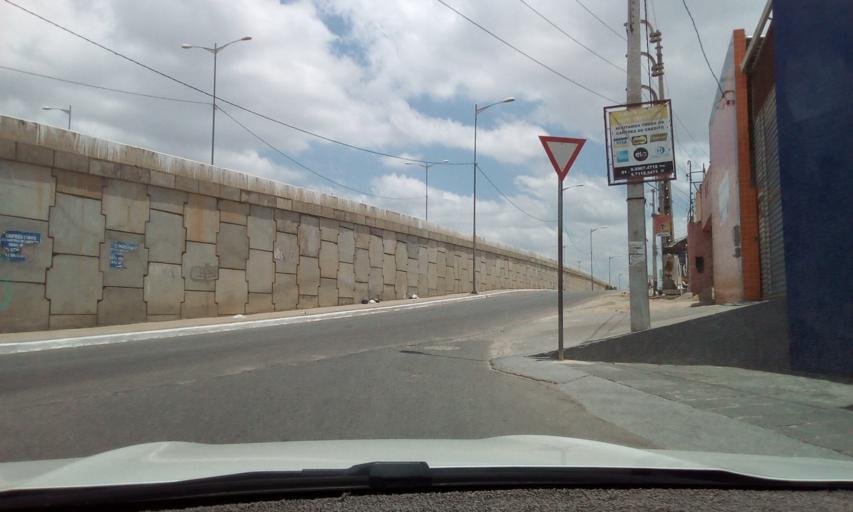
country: BR
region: Pernambuco
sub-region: Caruaru
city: Caruaru
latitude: -8.2735
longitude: -35.9826
